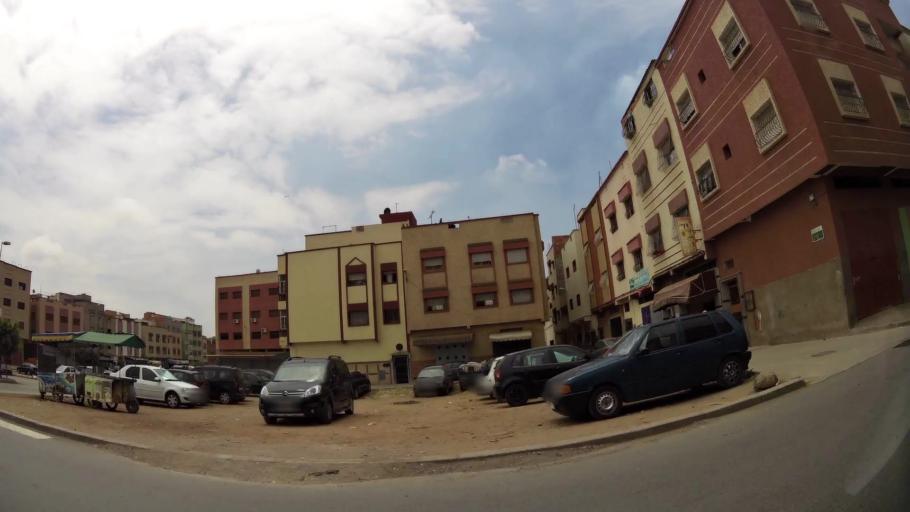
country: MA
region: Rabat-Sale-Zemmour-Zaer
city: Sale
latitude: 34.0573
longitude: -6.7858
